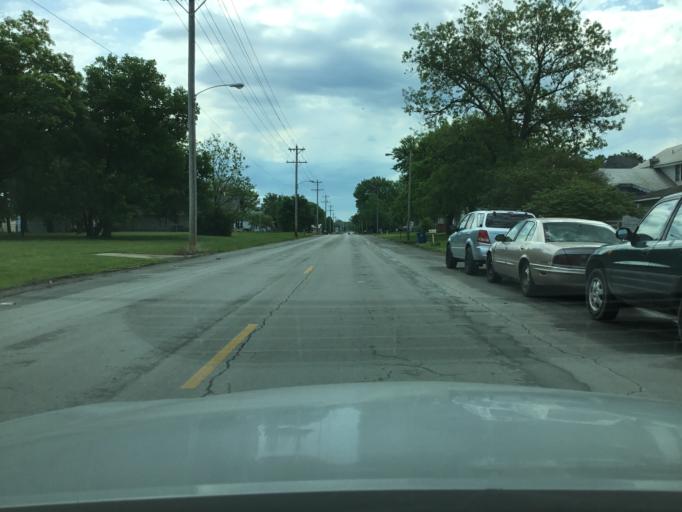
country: US
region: Kansas
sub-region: Montgomery County
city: Coffeyville
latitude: 37.0361
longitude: -95.6106
